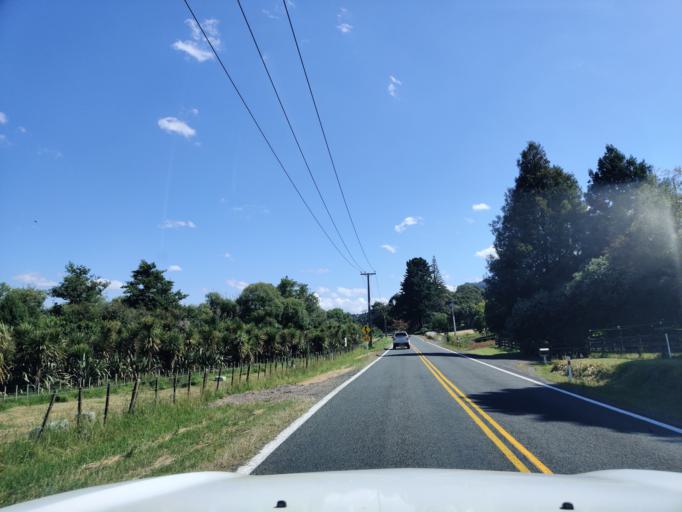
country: NZ
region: Waikato
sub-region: Waikato District
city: Ngaruawahia
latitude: -37.6497
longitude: 175.1453
